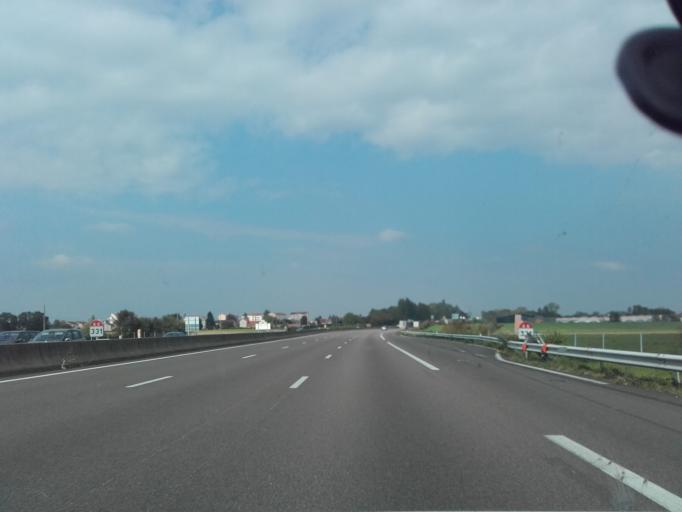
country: FR
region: Bourgogne
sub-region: Departement de Saone-et-Loire
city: Chatenoy-le-Royal
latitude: 46.7861
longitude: 4.8200
